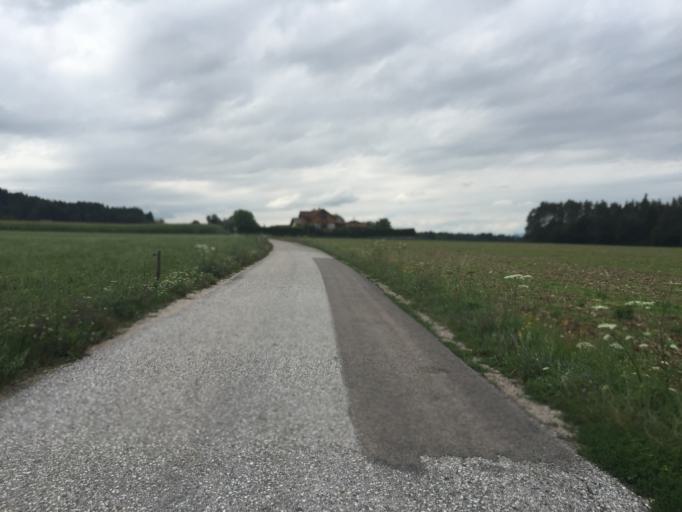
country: AT
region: Carinthia
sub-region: Politischer Bezirk Volkermarkt
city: Feistritz ob Bleiburg
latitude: 46.5556
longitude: 14.7837
